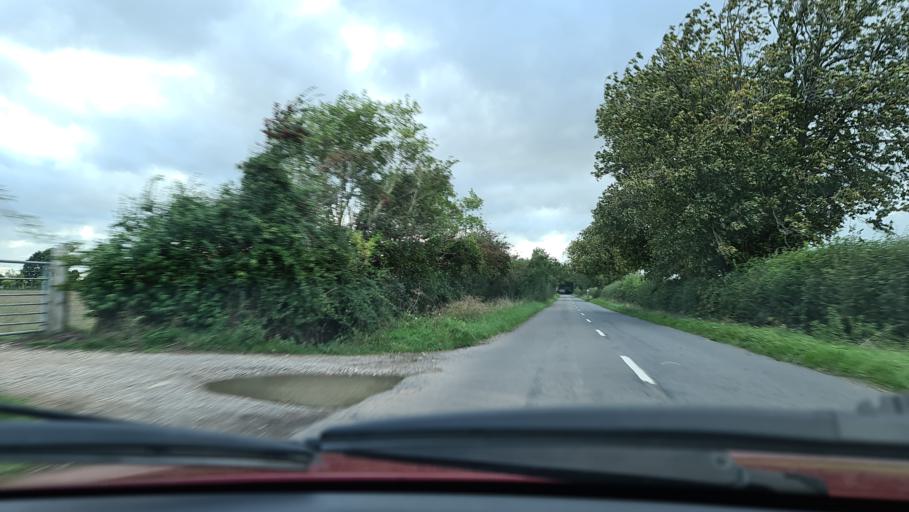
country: GB
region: England
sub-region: Buckinghamshire
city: Princes Risborough
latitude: 51.7420
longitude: -0.8252
